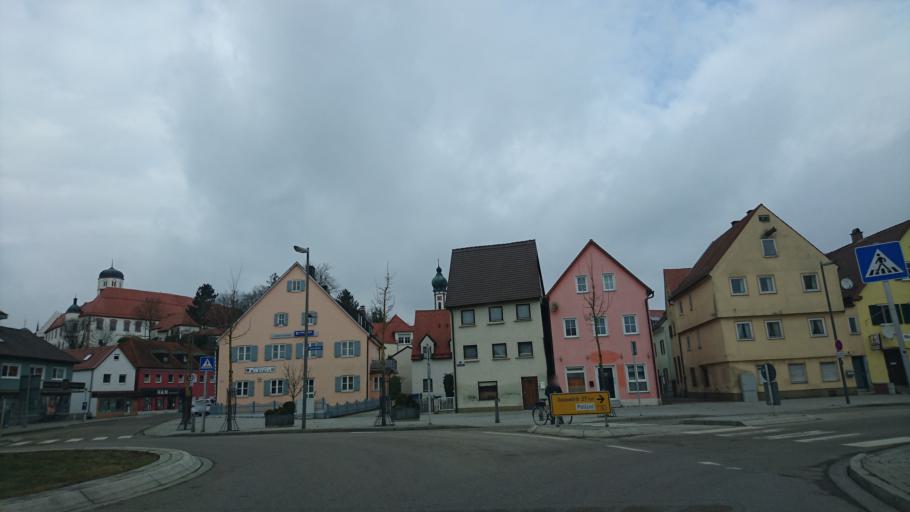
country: DE
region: Bavaria
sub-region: Swabia
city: Dillingen an der Donau
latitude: 48.5747
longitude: 10.4979
